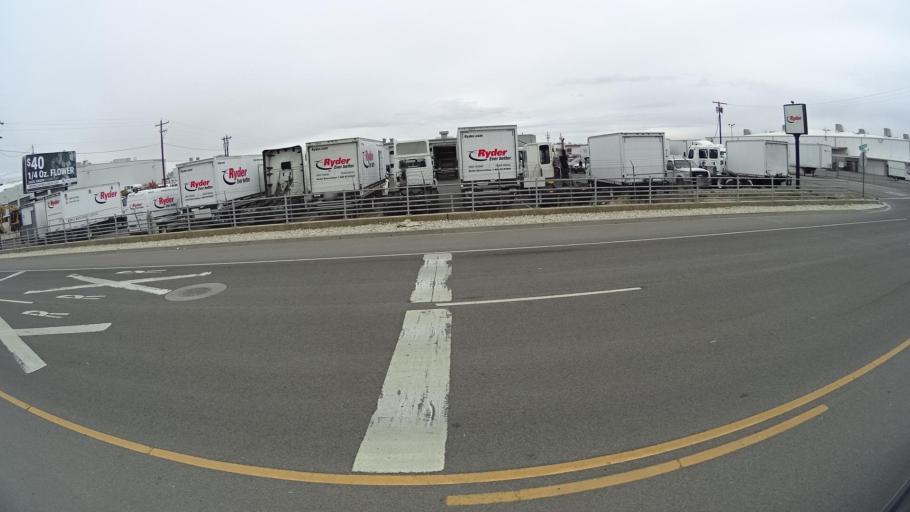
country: US
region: Nevada
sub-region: Washoe County
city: Sparks
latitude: 39.5274
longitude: -119.7488
